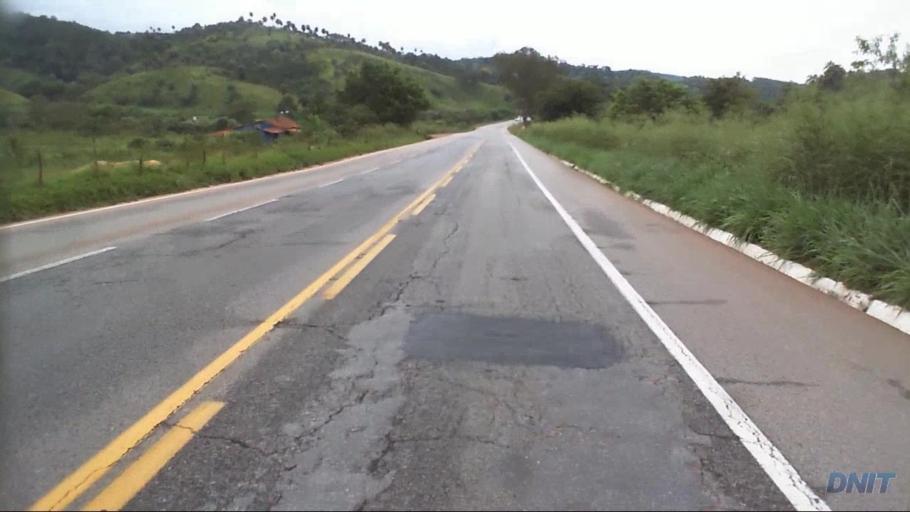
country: BR
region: Minas Gerais
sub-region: Barao De Cocais
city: Barao de Cocais
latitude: -19.8179
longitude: -43.3942
